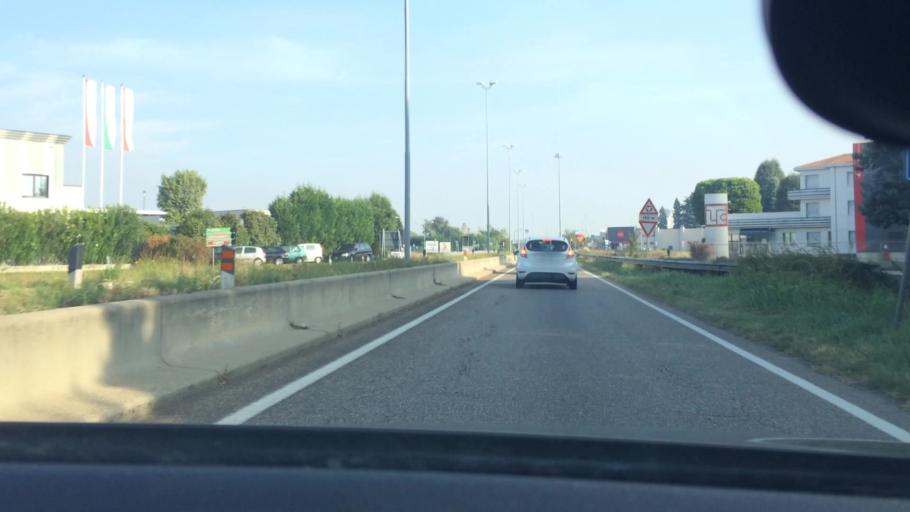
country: IT
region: Lombardy
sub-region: Citta metropolitana di Milano
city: Villa Cortese
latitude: 45.5695
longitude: 8.8993
